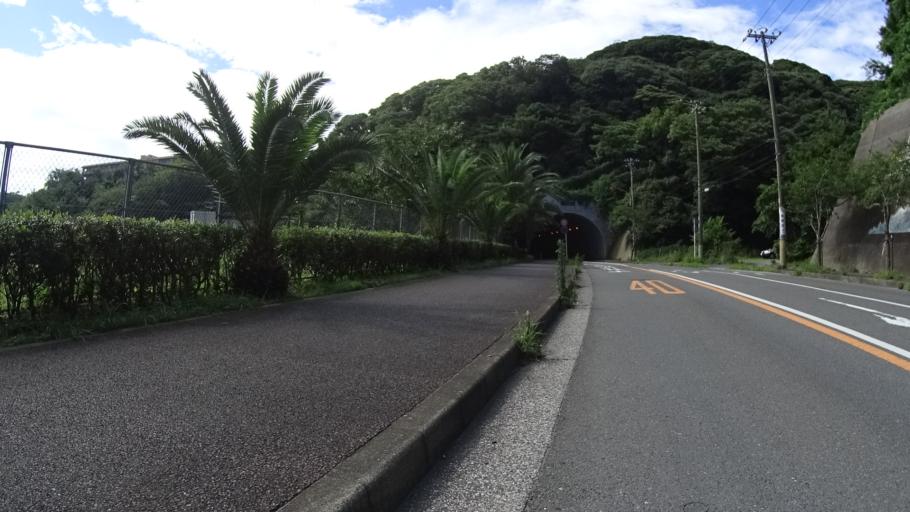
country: JP
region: Kanagawa
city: Yokosuka
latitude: 35.2337
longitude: 139.7220
